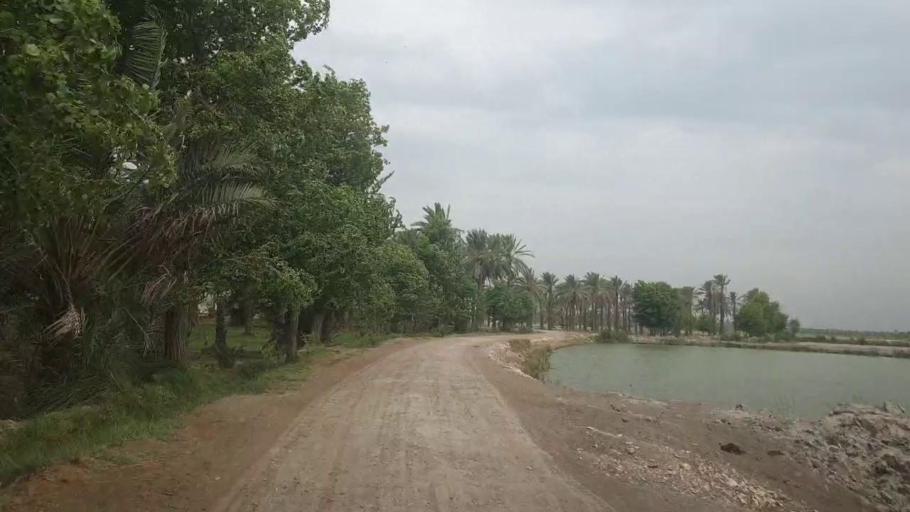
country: PK
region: Sindh
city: Khairpur
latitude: 27.5814
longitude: 68.7406
